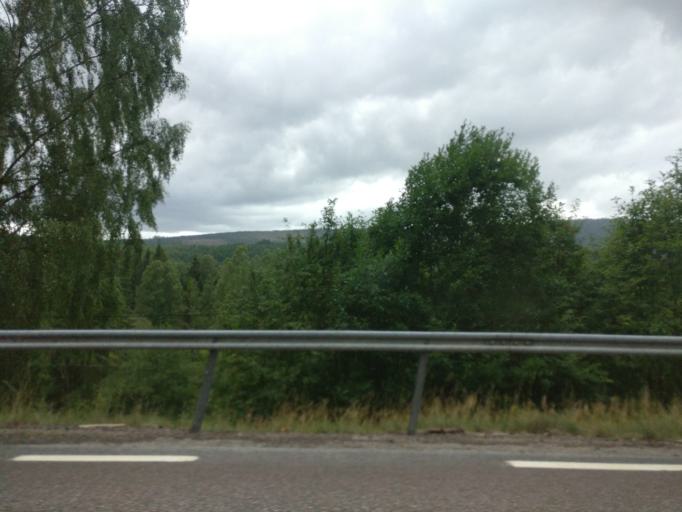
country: SE
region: Vaermland
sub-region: Torsby Kommun
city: Torsby
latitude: 60.6424
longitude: 13.0065
